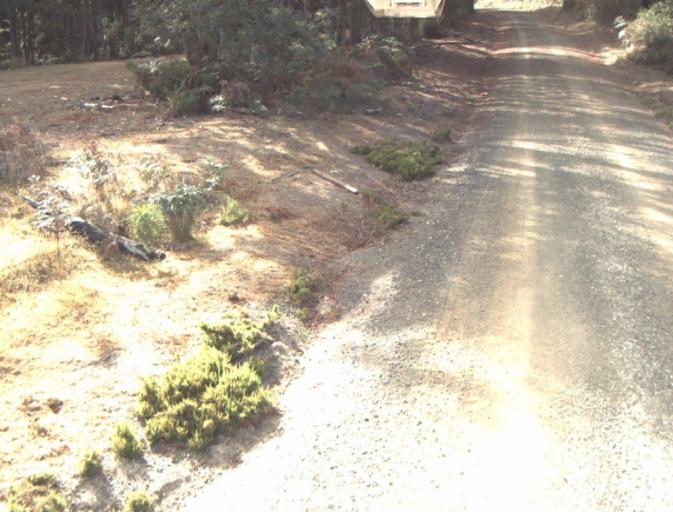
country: AU
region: Tasmania
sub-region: Launceston
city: Mayfield
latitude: -41.2944
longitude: 147.2179
